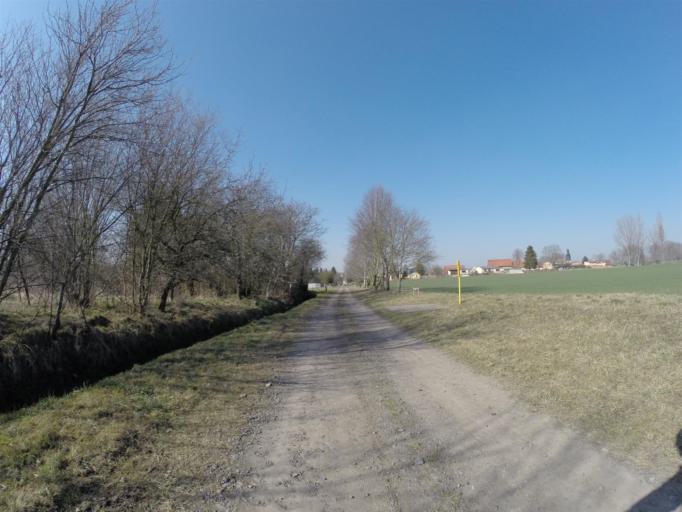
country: DE
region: Thuringia
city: Lehnstedt
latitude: 50.9365
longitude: 11.4394
